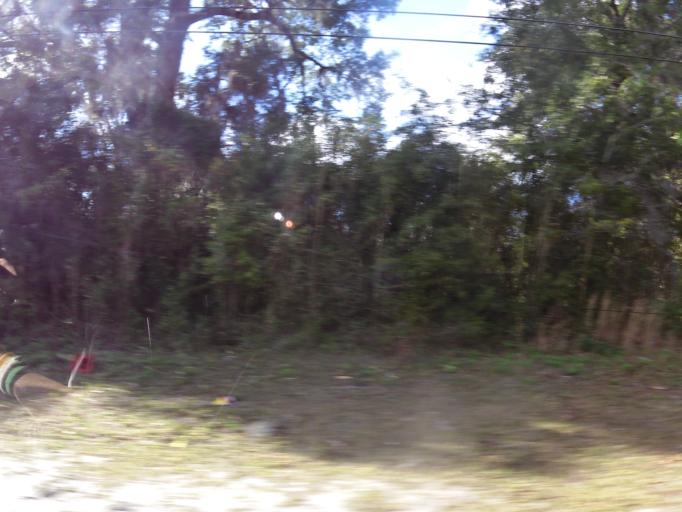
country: US
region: Florida
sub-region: Duval County
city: Jacksonville
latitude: 30.3314
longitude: -81.5602
